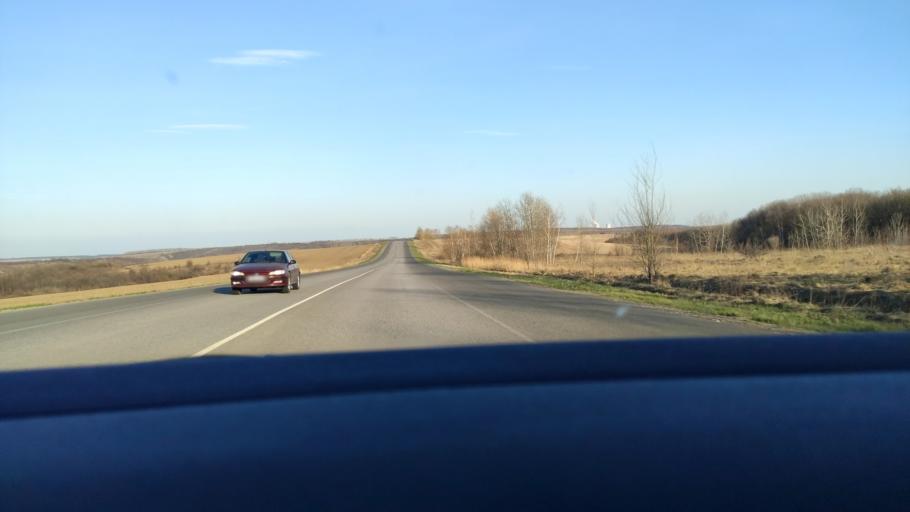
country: RU
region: Voronezj
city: Kolodeznyy
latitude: 51.3391
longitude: 39.0744
